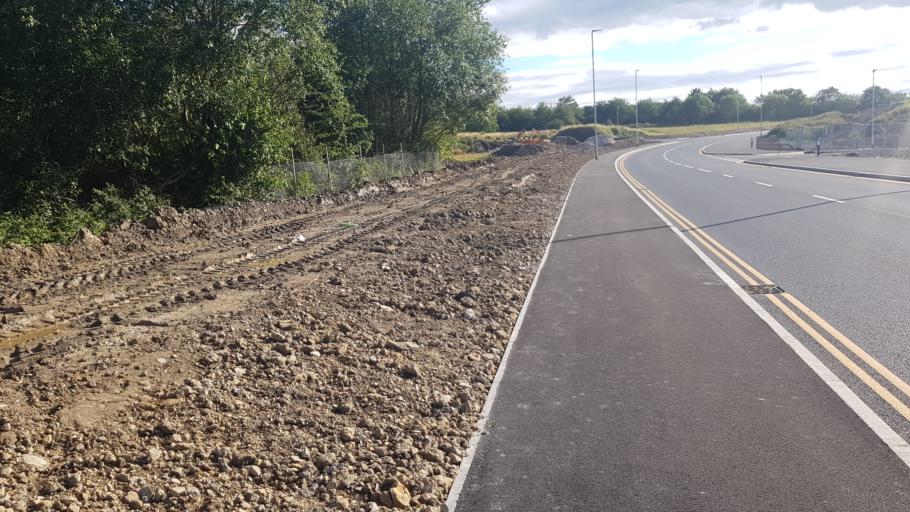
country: GB
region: England
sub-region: City and Borough of Wakefield
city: Castleford
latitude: 53.7065
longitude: -1.3558
